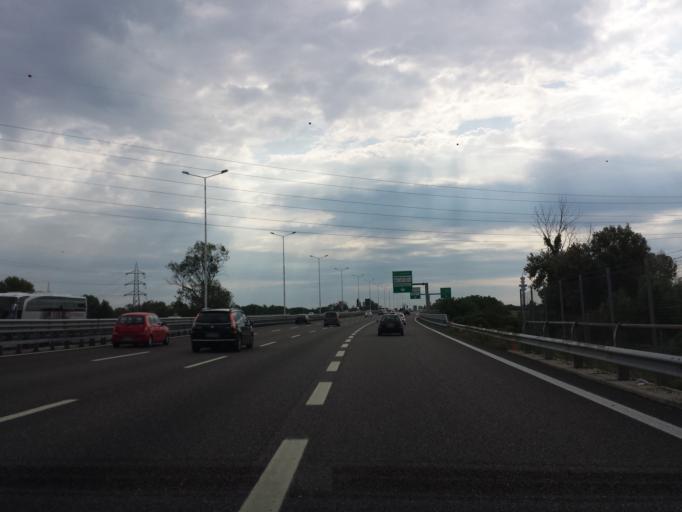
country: IT
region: Lombardy
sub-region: Citta metropolitana di Milano
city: Assago
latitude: 45.3972
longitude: 9.1355
